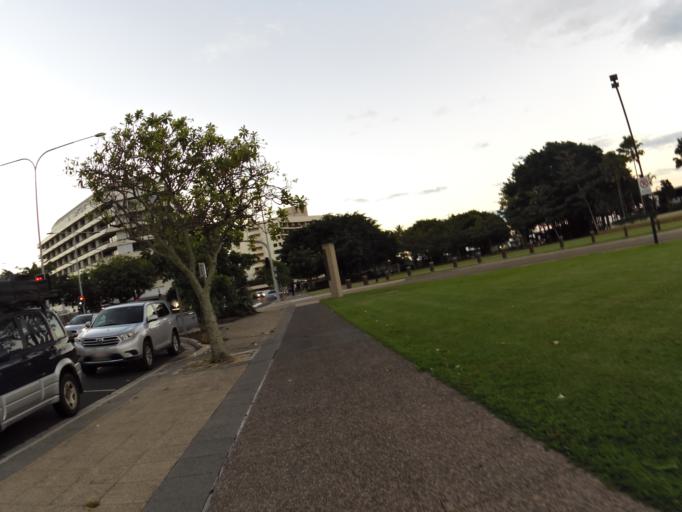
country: AU
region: Queensland
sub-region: Cairns
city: Cairns
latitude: -16.9251
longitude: 145.7798
